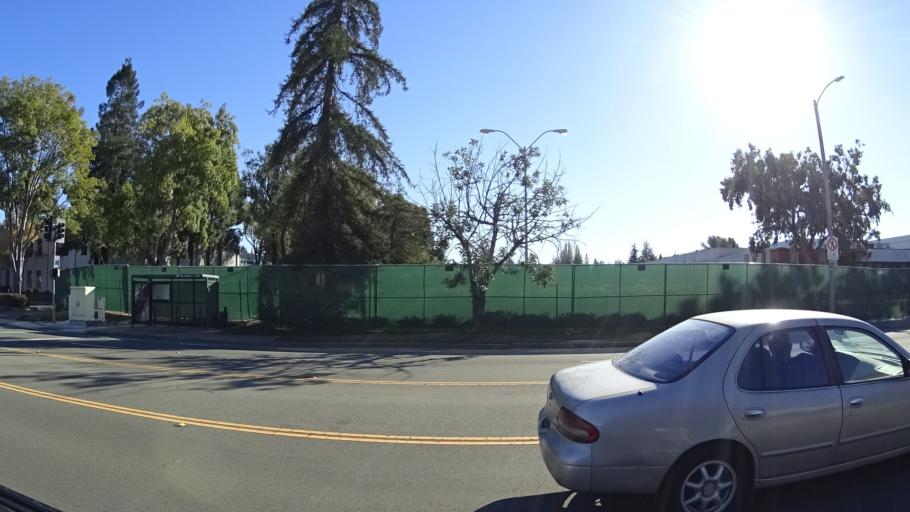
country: US
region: California
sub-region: Santa Clara County
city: Sunnyvale
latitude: 37.3739
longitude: -122.0020
